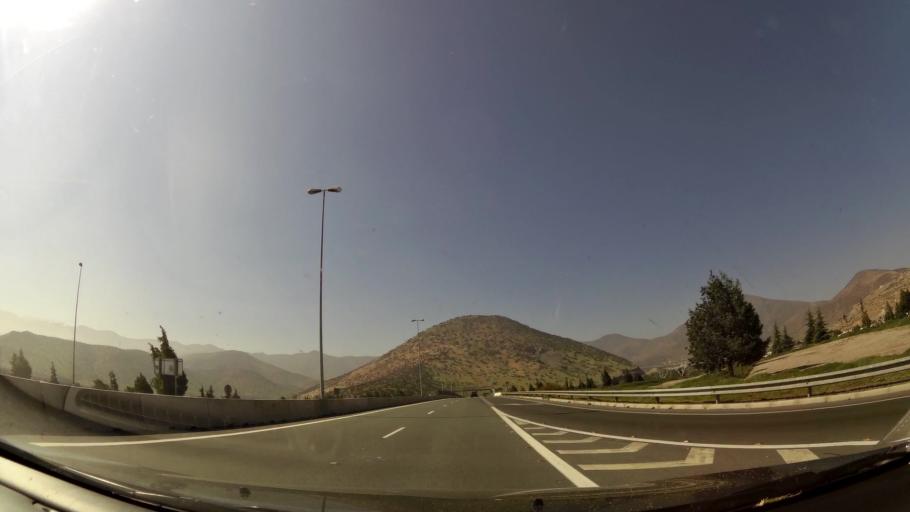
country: CL
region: Santiago Metropolitan
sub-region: Provincia de Chacabuco
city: Chicureo Abajo
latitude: -33.3004
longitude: -70.6611
